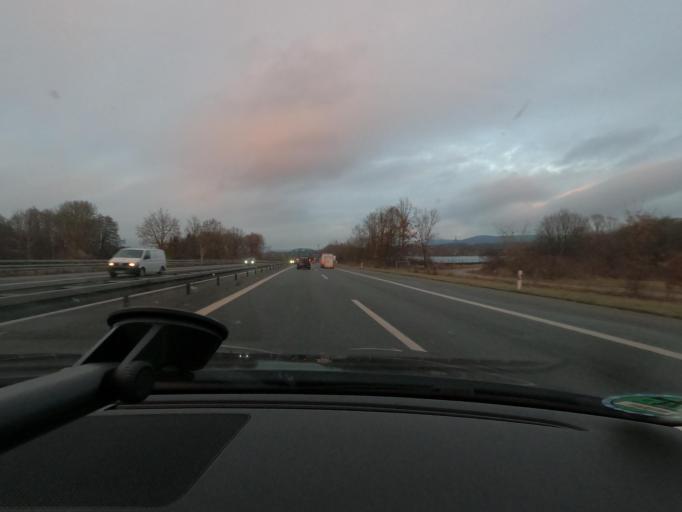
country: DE
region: Bavaria
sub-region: Upper Franconia
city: Forchheim
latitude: 49.7424
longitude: 11.0562
